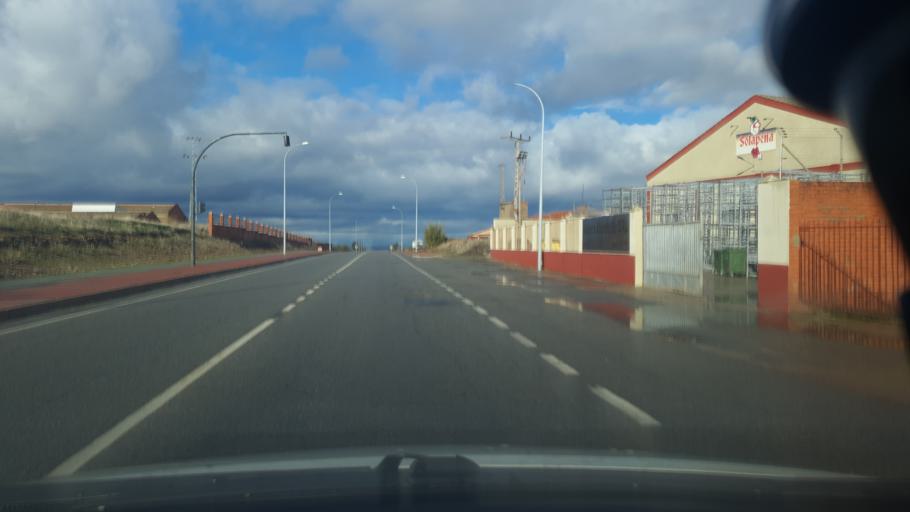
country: ES
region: Castille and Leon
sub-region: Provincia de Segovia
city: Carbonero el Mayor
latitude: 41.1270
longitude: -4.2686
